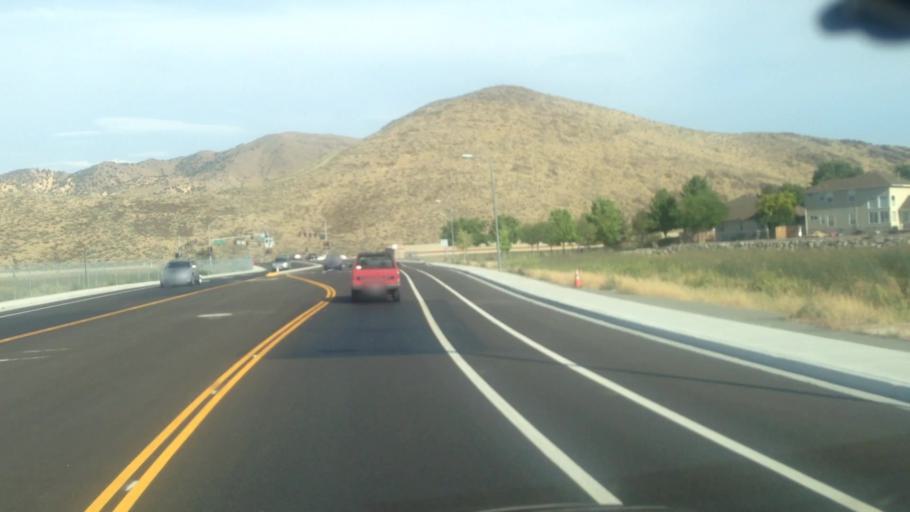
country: US
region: Nevada
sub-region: Washoe County
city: Sparks
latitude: 39.4857
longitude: -119.7392
